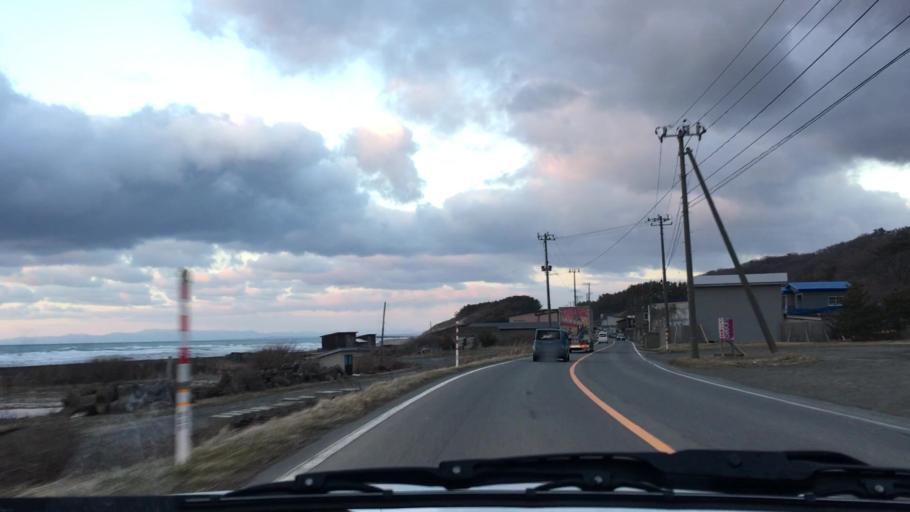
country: JP
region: Aomori
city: Shimokizukuri
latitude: 40.7536
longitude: 140.1486
